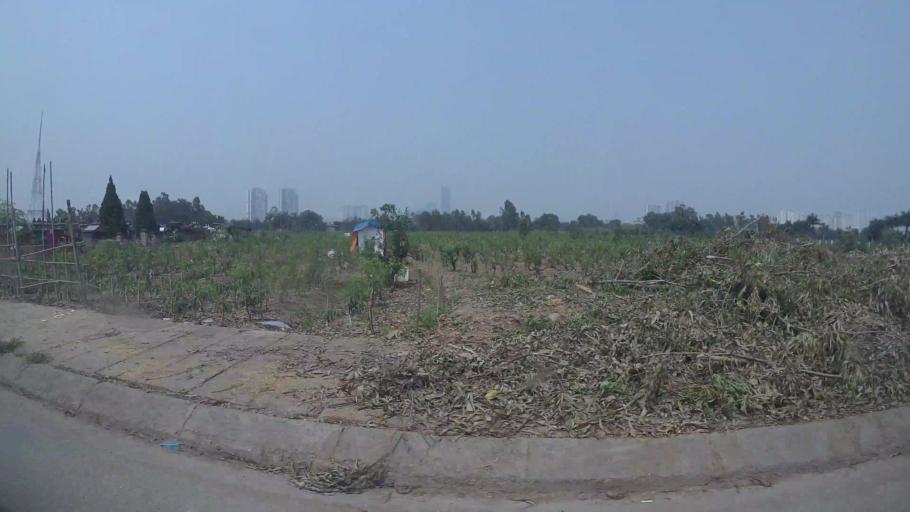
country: VN
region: Ha Noi
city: Ha Dong
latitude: 20.9933
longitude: 105.7670
